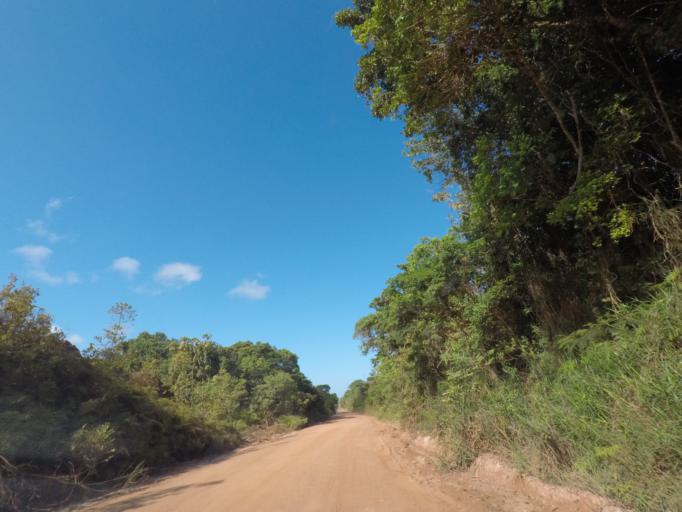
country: BR
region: Bahia
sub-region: Marau
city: Marau
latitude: -14.1290
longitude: -38.9938
